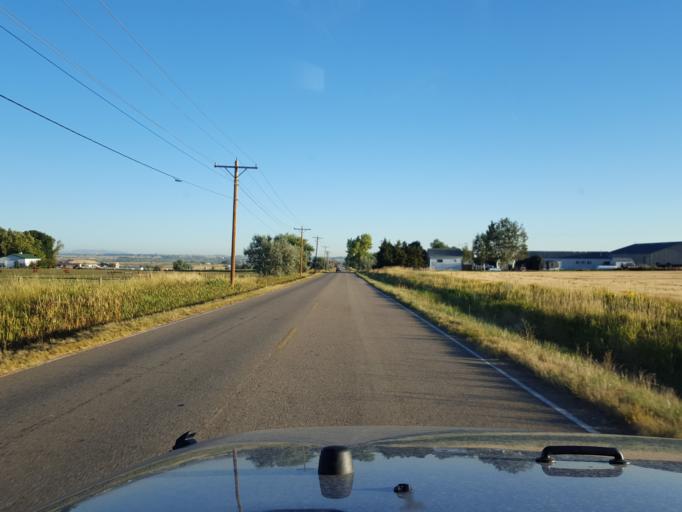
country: US
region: Colorado
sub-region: Weld County
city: Firestone
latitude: 40.1134
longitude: -104.9988
